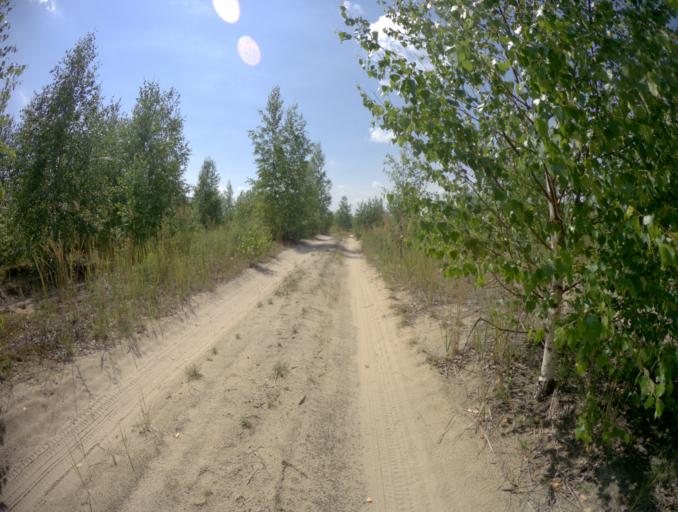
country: RU
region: Ivanovo
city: Talitsy
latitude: 56.4917
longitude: 42.1932
